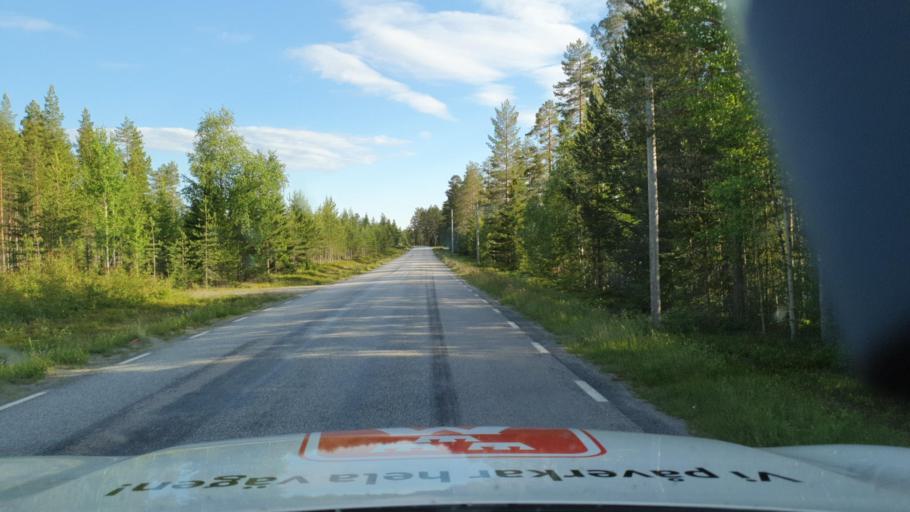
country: SE
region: Vaesterbotten
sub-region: Umea Kommun
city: Roback
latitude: 63.9236
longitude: 20.1453
